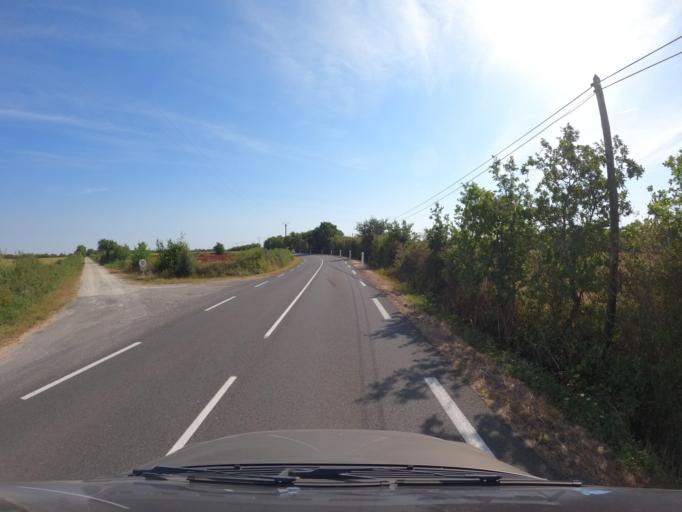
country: FR
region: Pays de la Loire
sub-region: Departement de la Vendee
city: Froidfond
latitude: 46.8517
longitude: -1.7259
